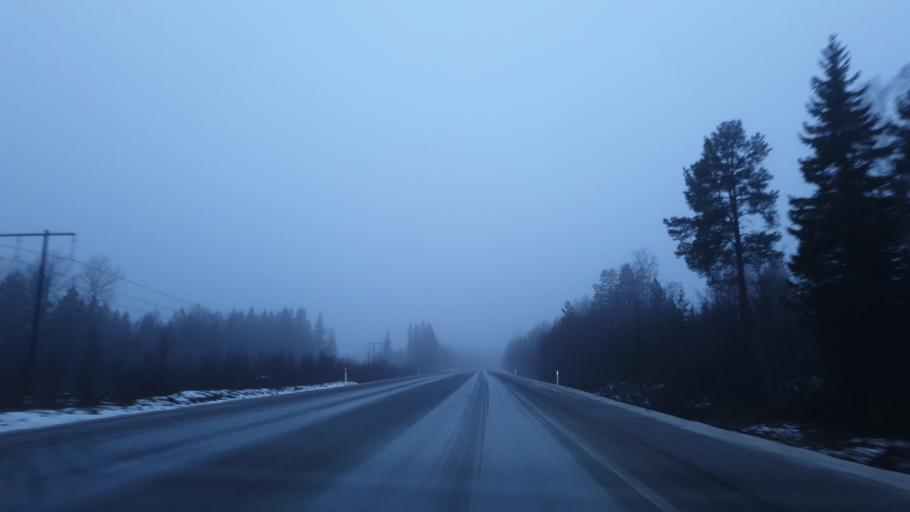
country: SE
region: Vaesterbotten
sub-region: Umea Kommun
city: Holmsund
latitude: 63.7517
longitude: 20.3675
